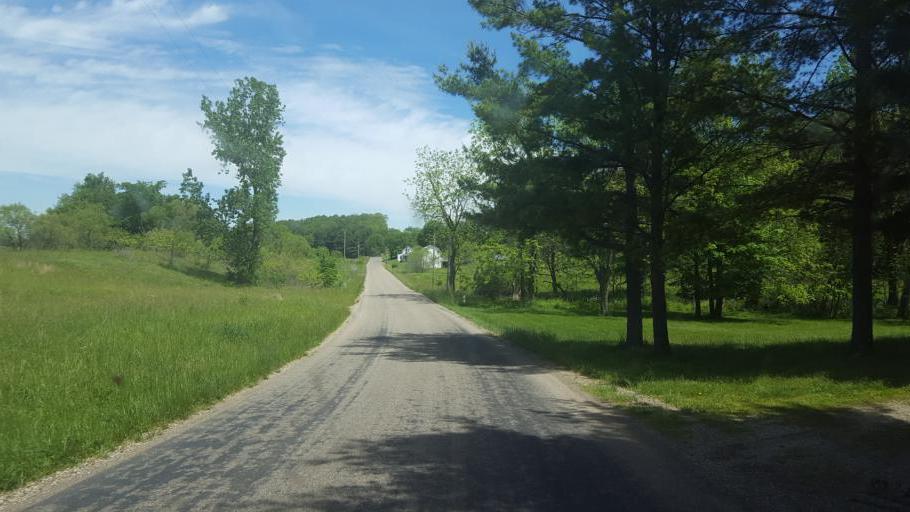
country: US
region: Ohio
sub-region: Knox County
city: Oak Hill
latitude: 40.3705
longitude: -82.3105
